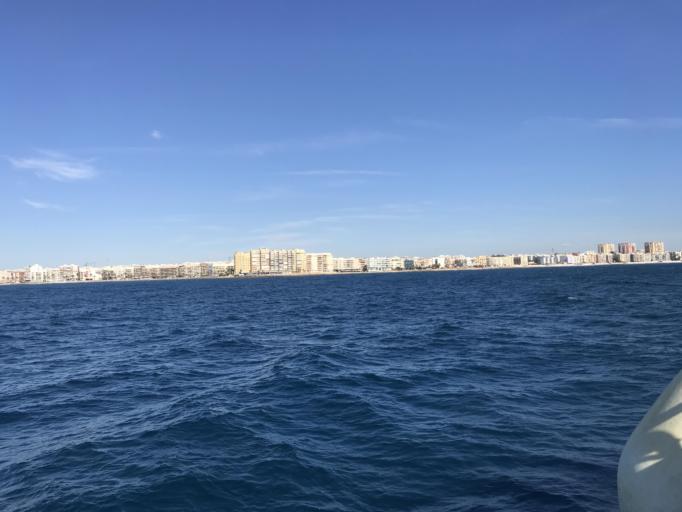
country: ES
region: Valencia
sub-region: Provincia de Alicante
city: Torrevieja
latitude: 37.9701
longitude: -0.6609
